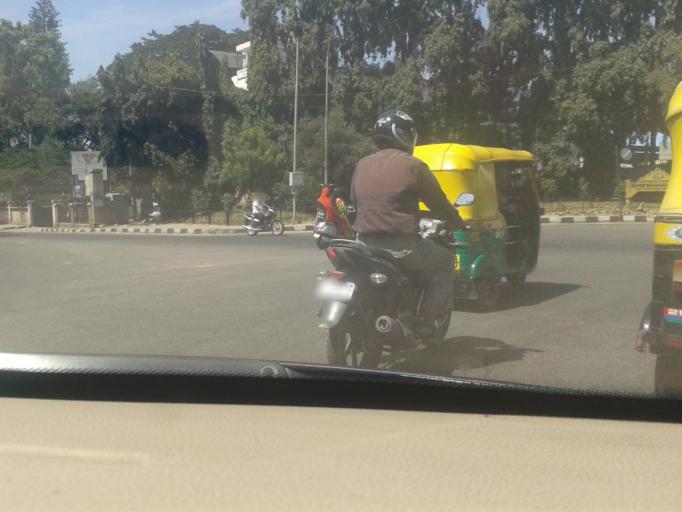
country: IN
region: Karnataka
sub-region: Bangalore Urban
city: Bangalore
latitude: 12.9515
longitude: 77.5905
